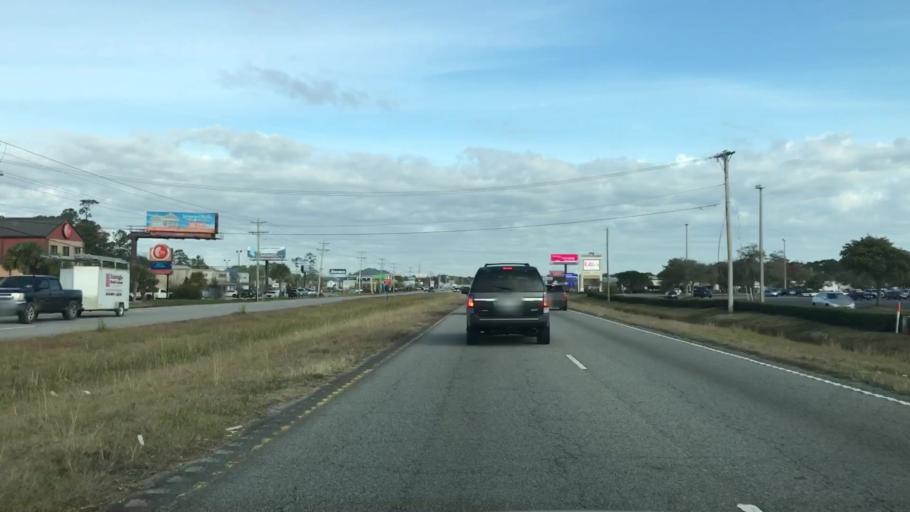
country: US
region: South Carolina
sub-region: Horry County
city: Garden City
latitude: 33.5804
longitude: -79.0282
